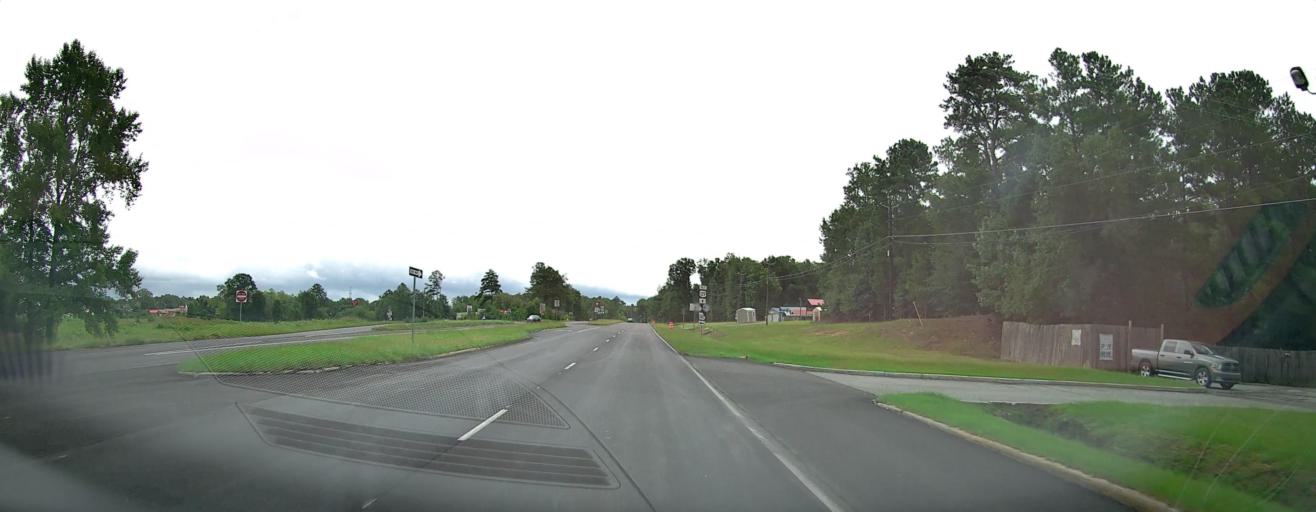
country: US
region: Georgia
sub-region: Bibb County
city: Macon
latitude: 32.8401
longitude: -83.5812
